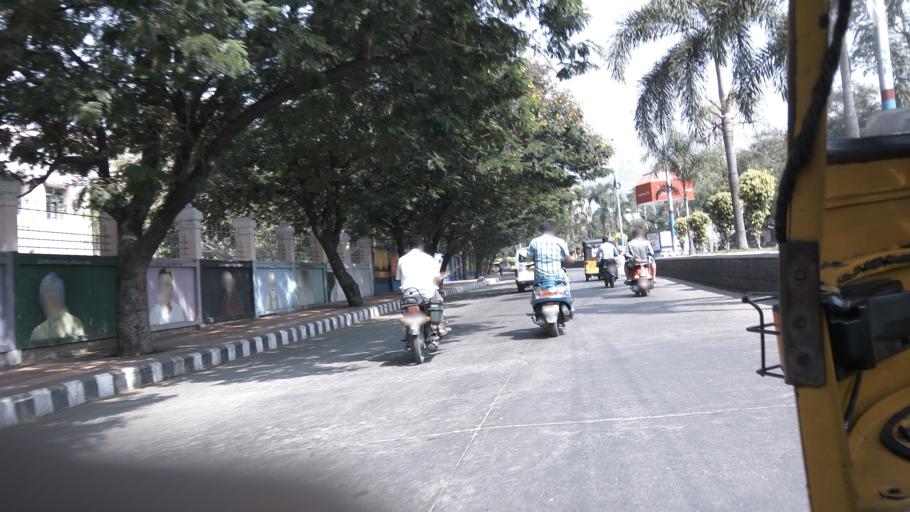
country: IN
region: Andhra Pradesh
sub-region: Chittoor
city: Tirupati
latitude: 13.6400
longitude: 79.4101
